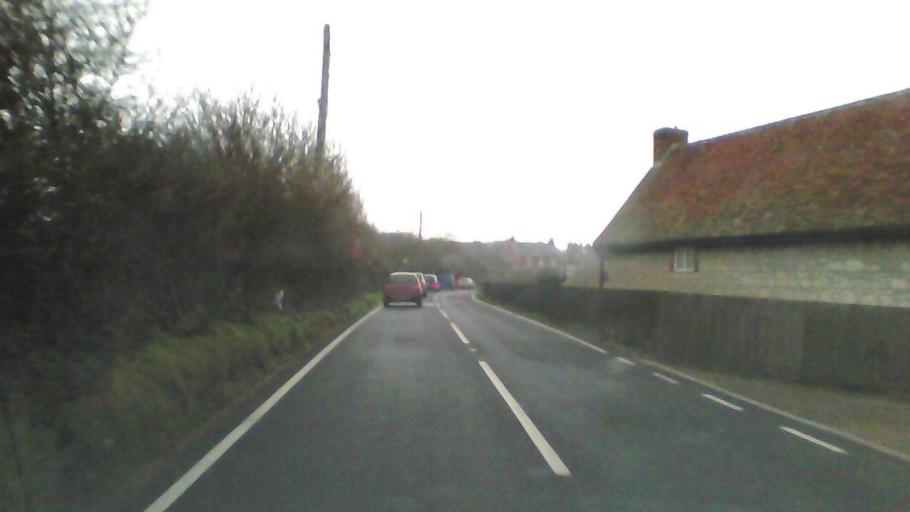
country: GB
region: England
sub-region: Isle of Wight
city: Newport
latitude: 50.6900
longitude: -1.2494
